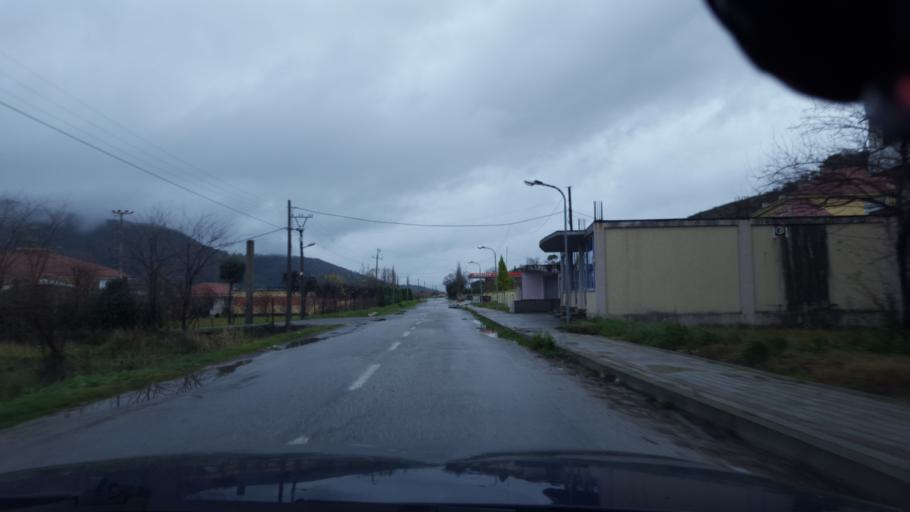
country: AL
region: Shkoder
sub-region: Rrethi i Shkodres
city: Berdica e Madhe
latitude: 42.0166
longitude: 19.4846
